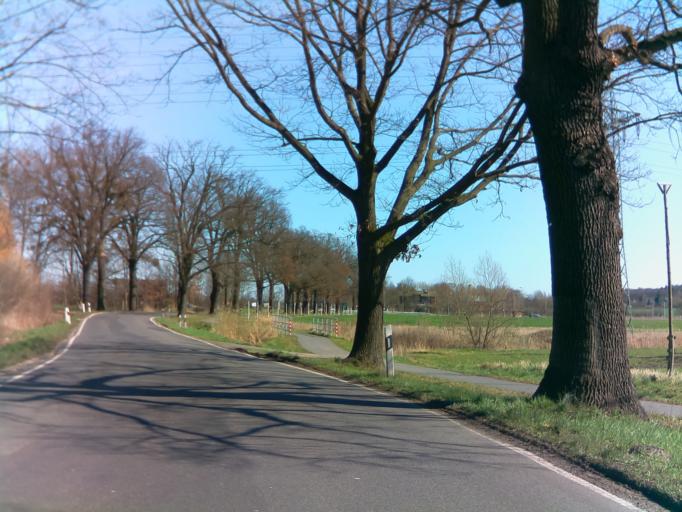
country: DE
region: Brandenburg
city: Werder
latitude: 52.4306
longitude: 12.9670
